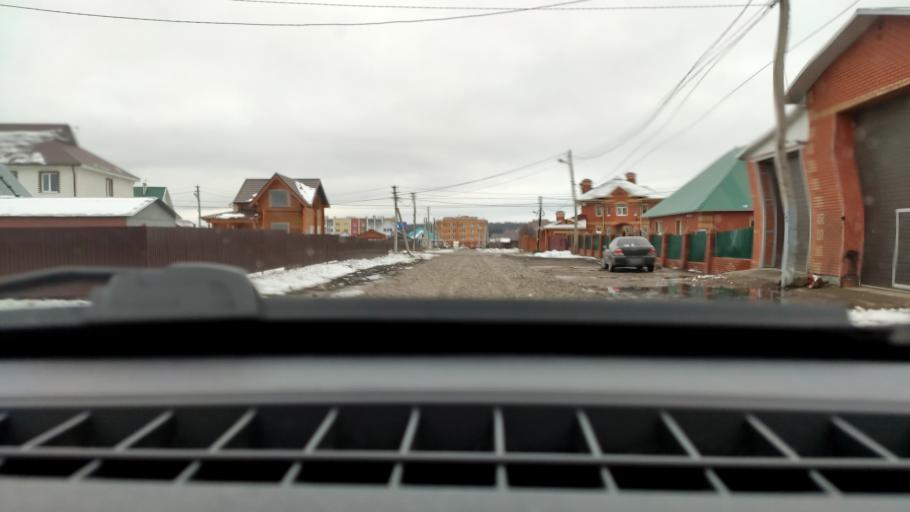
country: RU
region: Bashkortostan
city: Mikhaylovka
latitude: 54.8100
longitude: 55.7962
